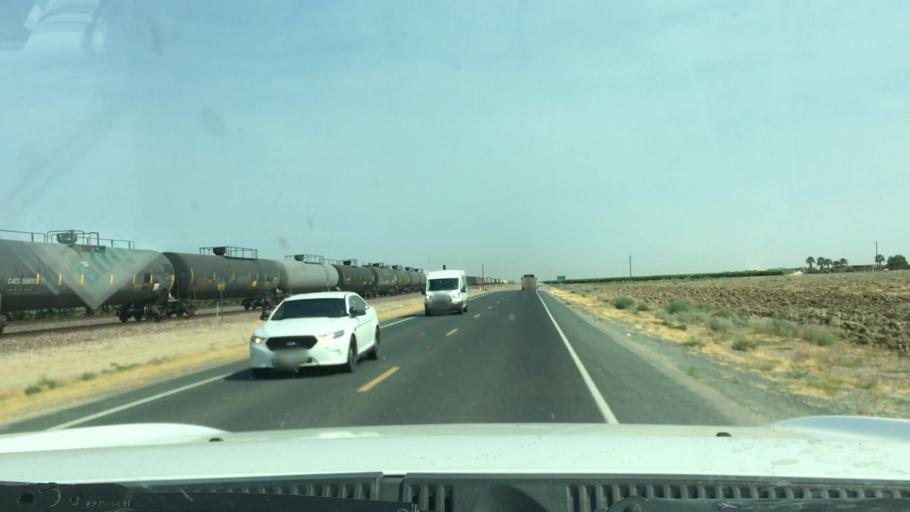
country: US
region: California
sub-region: Kern County
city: Delano
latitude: 35.7722
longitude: -119.3489
